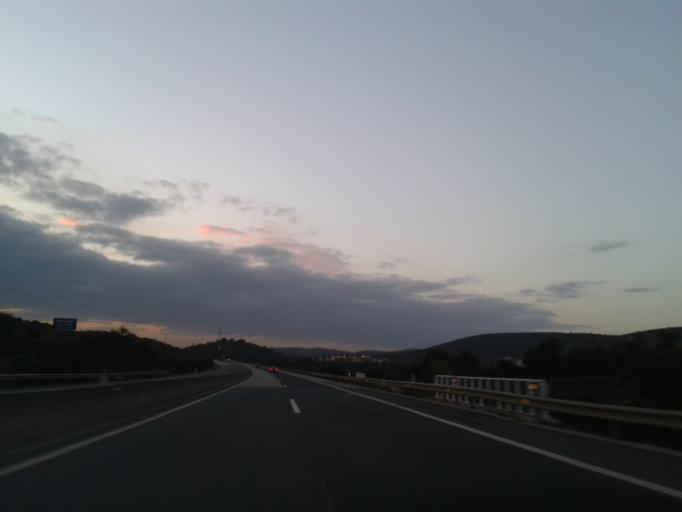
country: PT
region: Faro
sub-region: Loule
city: Vilamoura
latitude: 37.1279
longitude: -8.0931
